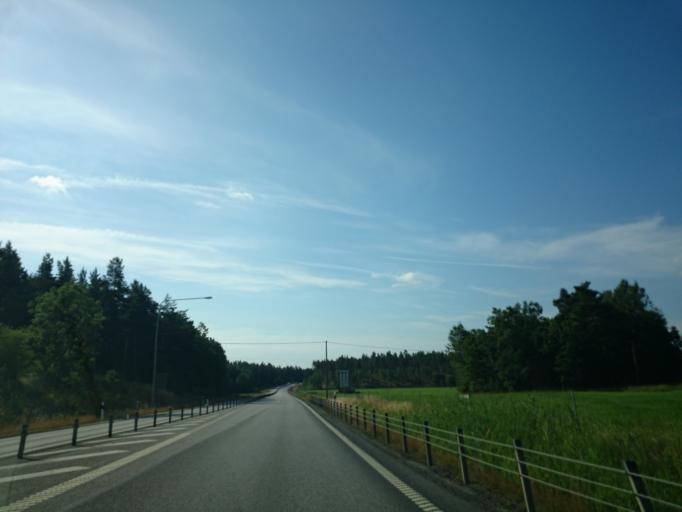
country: SE
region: OEstergoetland
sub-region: Soderkopings Kommun
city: Soederkoeping
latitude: 58.4398
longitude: 16.3732
